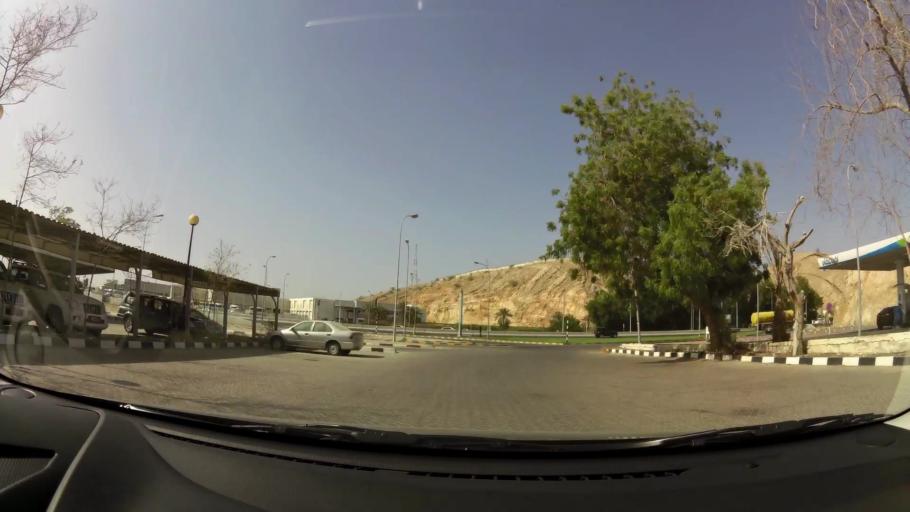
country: OM
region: Muhafazat Masqat
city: Muscat
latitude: 23.6072
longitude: 58.5012
